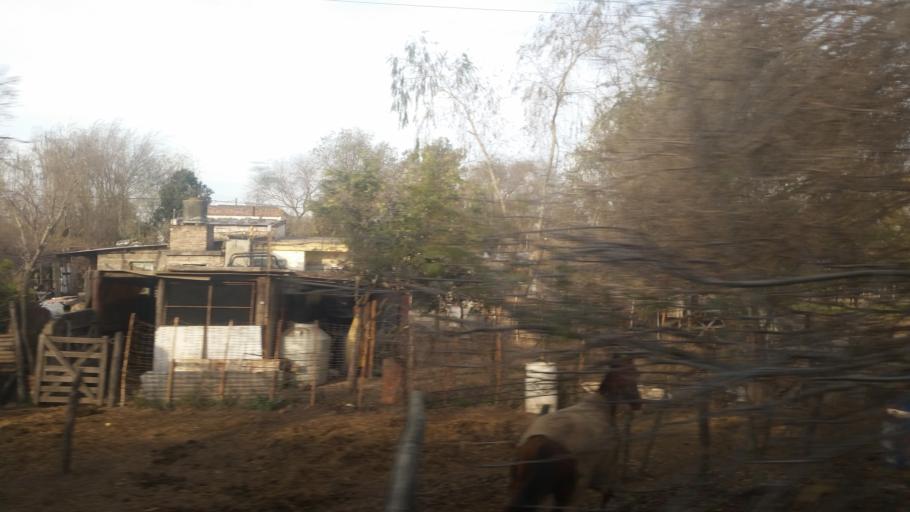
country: AR
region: Cordoba
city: Leones
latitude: -32.6315
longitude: -62.4857
